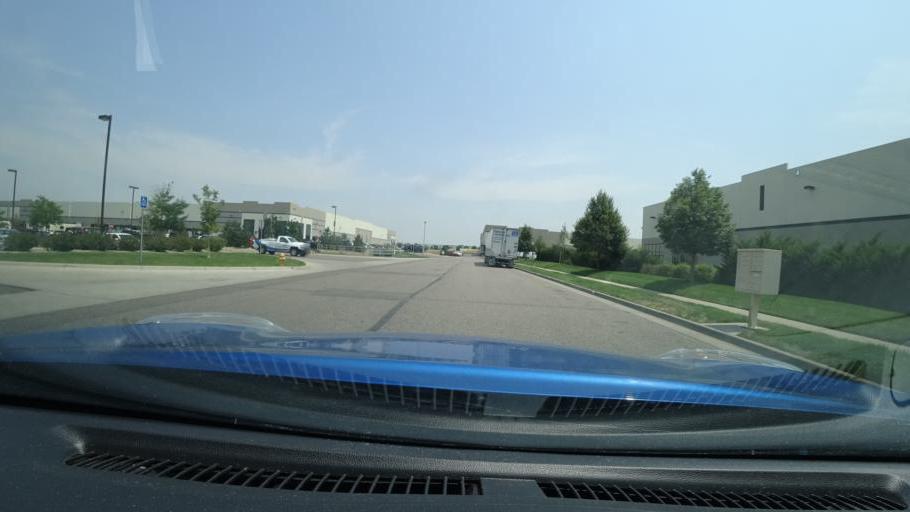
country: US
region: Colorado
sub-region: Adams County
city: Aurora
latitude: 39.7660
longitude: -104.7580
